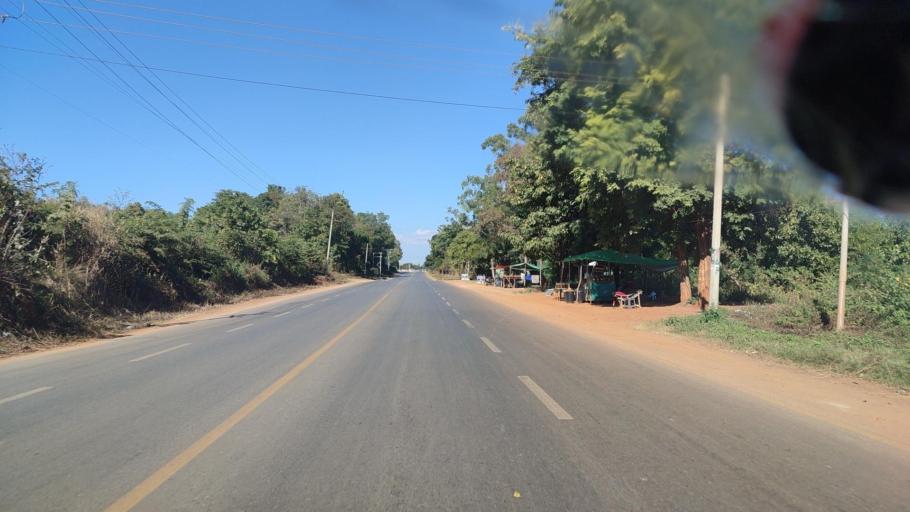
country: MM
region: Mandalay
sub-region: Pyin Oo Lwin District
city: Pyin Oo Lwin
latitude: 22.0980
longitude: 96.5973
